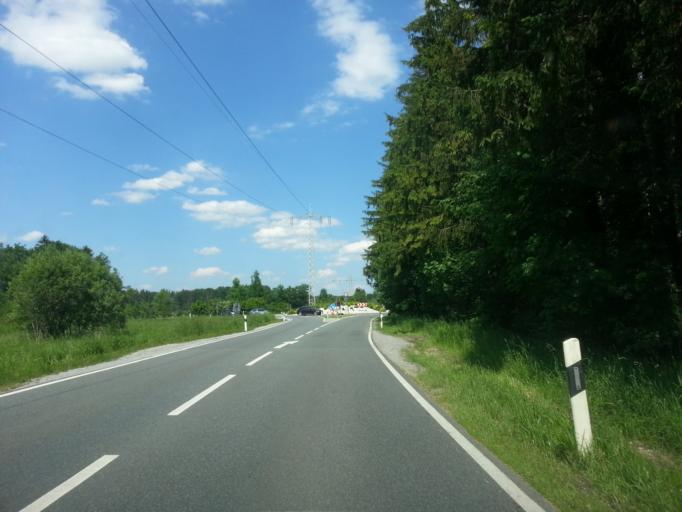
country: DE
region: Bavaria
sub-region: Upper Bavaria
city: Bad Feilnbach
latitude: 47.8089
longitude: 12.0172
